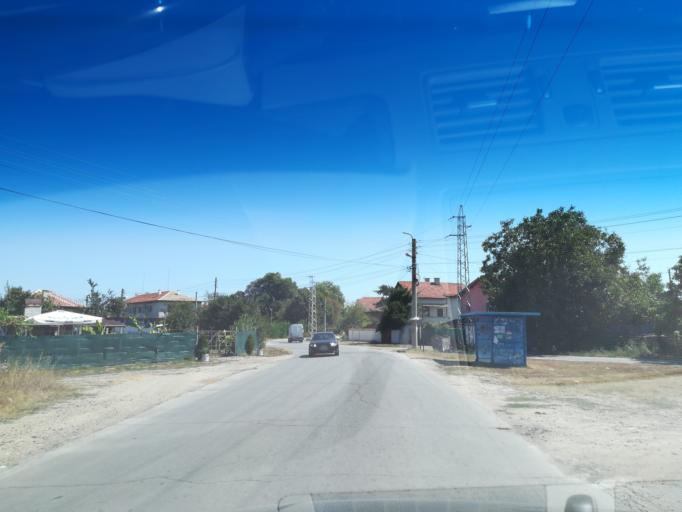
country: BG
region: Pazardzhik
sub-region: Obshtina Pazardzhik
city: Pazardzhik
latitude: 42.2512
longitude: 24.4251
